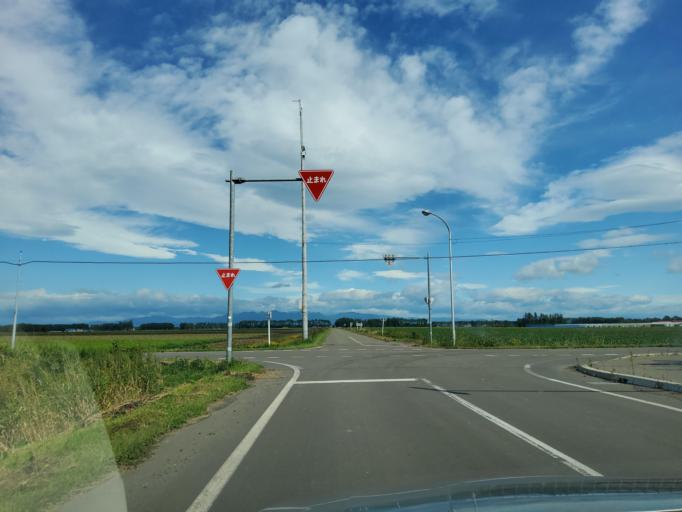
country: JP
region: Hokkaido
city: Otofuke
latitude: 42.9901
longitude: 143.1757
